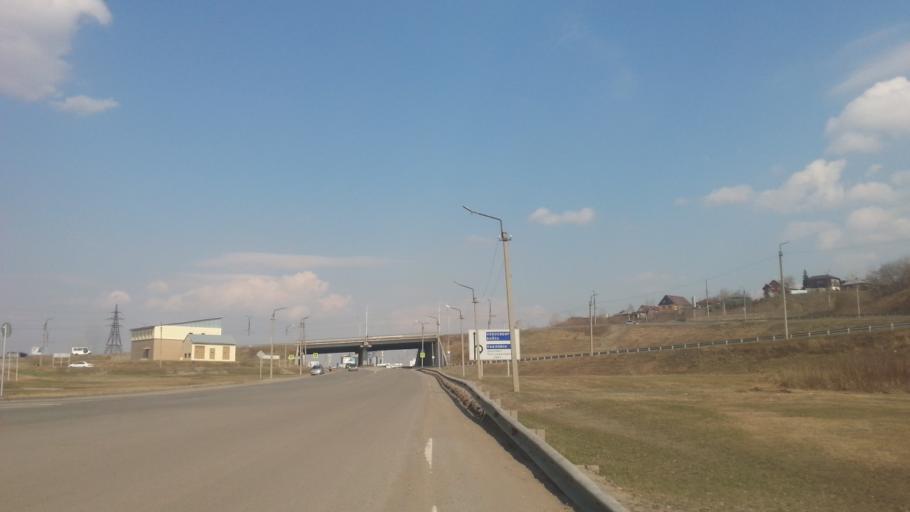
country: RU
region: Altai Krai
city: Zaton
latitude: 53.3221
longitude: 83.7841
